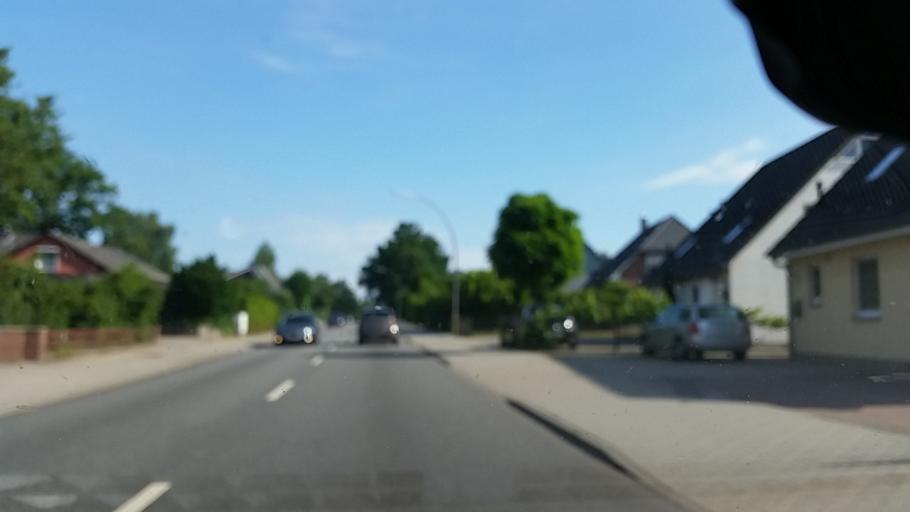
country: DE
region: Hamburg
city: Langenhorn
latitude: 53.7024
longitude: 10.0280
